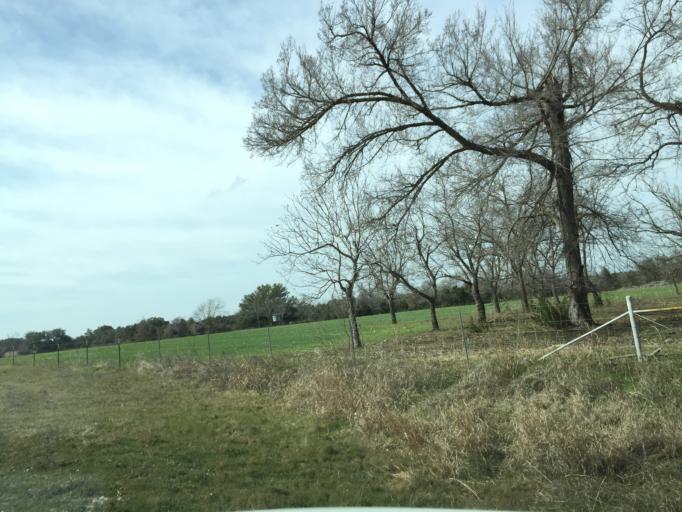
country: US
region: Texas
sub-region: Gillespie County
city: Fredericksburg
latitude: 30.3945
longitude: -98.7090
